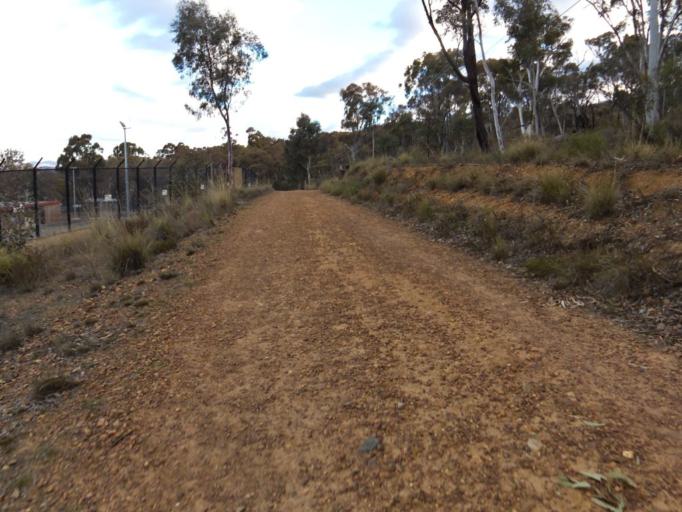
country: AU
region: Australian Capital Territory
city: Acton
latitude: -35.2691
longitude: 149.1085
